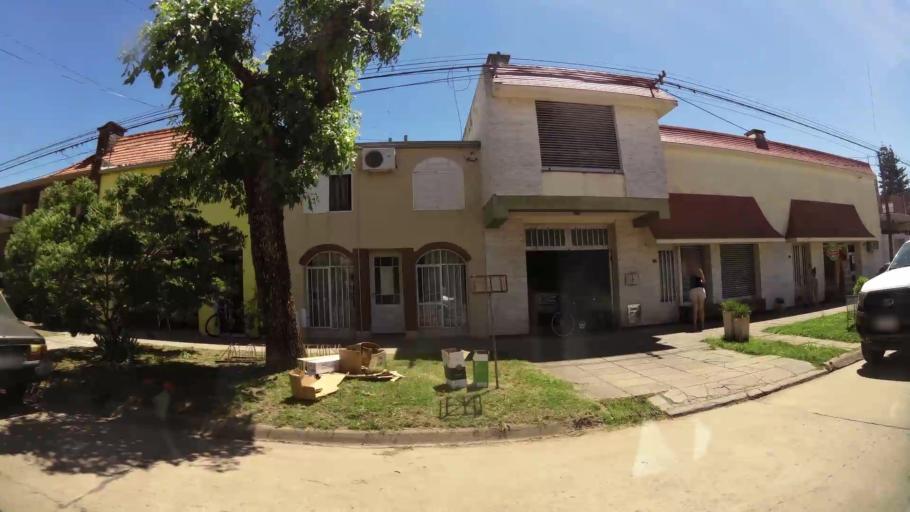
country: AR
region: Santa Fe
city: Esperanza
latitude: -31.4023
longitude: -61.0843
